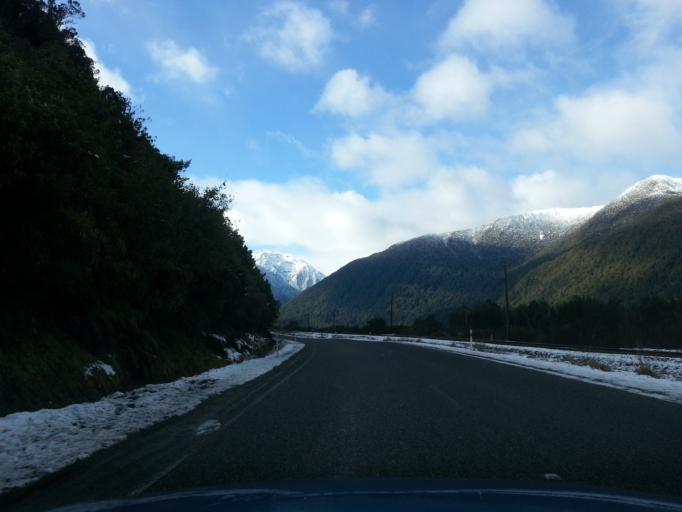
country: NZ
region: West Coast
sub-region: Grey District
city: Greymouth
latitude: -42.7901
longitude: 171.5986
